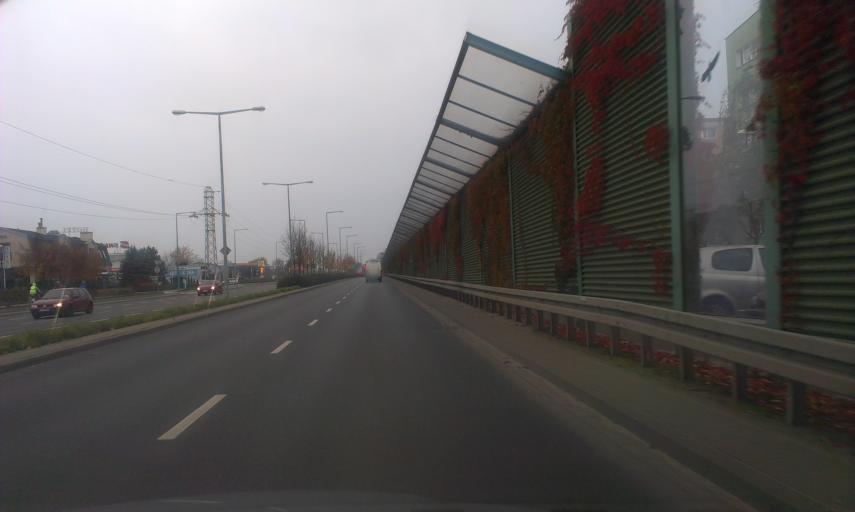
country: PL
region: Greater Poland Voivodeship
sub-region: Poznan
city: Poznan
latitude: 52.4085
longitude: 16.8683
